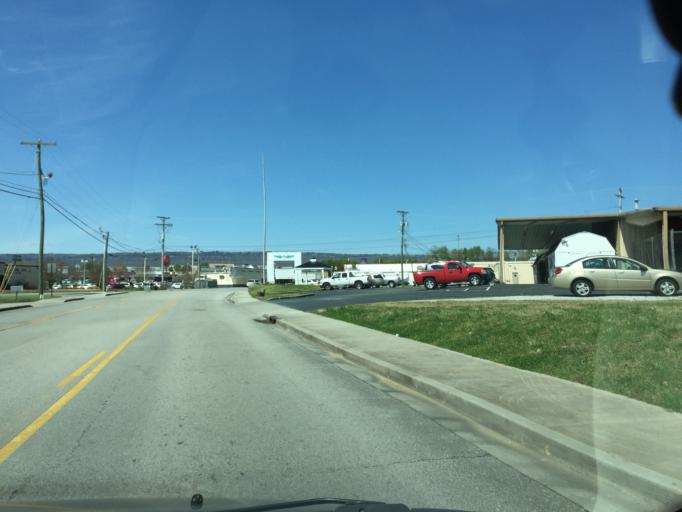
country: US
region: Tennessee
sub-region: Hamilton County
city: Red Bank
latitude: 35.1346
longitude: -85.2376
